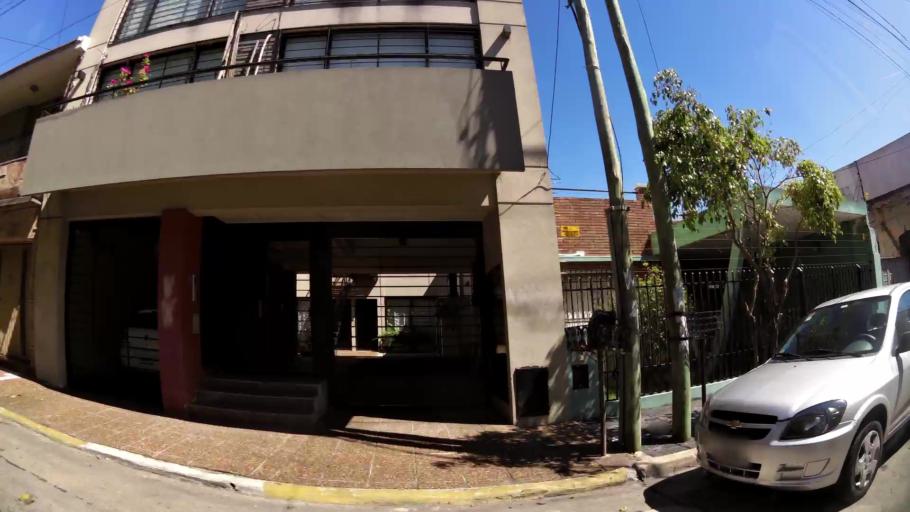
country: AR
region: Buenos Aires
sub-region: Partido de Quilmes
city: Quilmes
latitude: -34.7062
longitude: -58.2834
